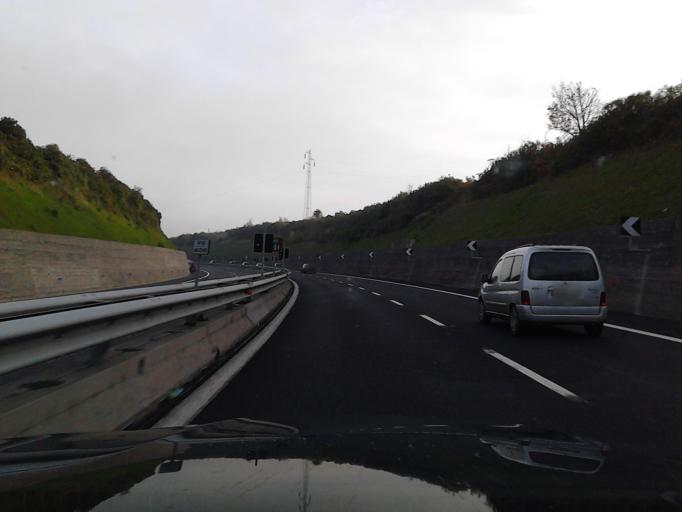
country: IT
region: Abruzzo
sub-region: Provincia di Chieti
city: San Vito Chietino
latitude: 42.3024
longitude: 14.4229
